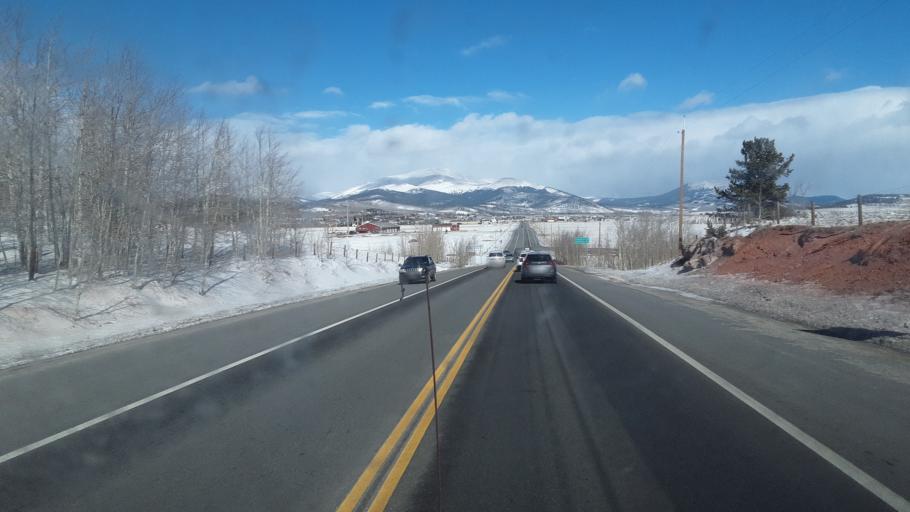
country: US
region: Colorado
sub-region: Park County
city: Fairplay
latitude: 39.2034
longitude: -105.9952
